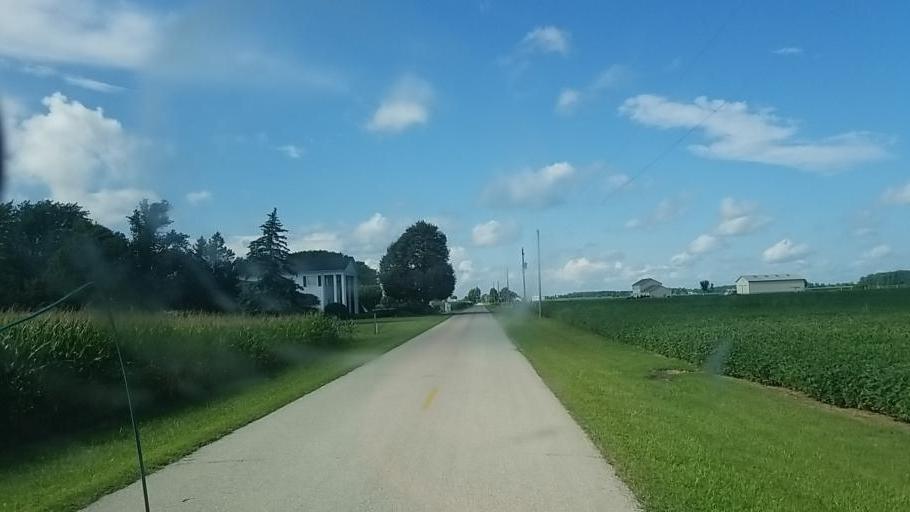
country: US
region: Ohio
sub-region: Hardin County
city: Forest
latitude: 40.7039
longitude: -83.5142
